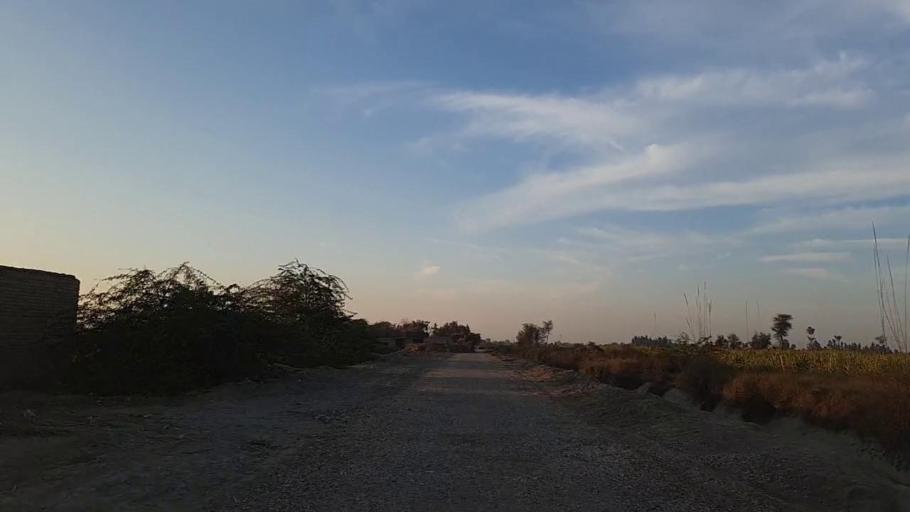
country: PK
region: Sindh
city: Bandhi
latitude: 26.6140
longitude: 68.3563
